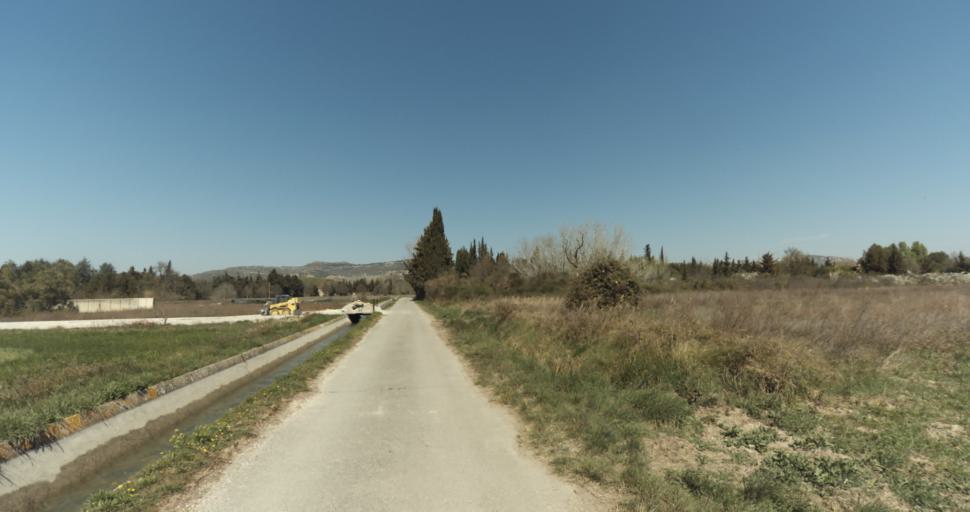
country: FR
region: Provence-Alpes-Cote d'Azur
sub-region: Departement des Bouches-du-Rhone
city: Pelissanne
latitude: 43.6253
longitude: 5.1459
